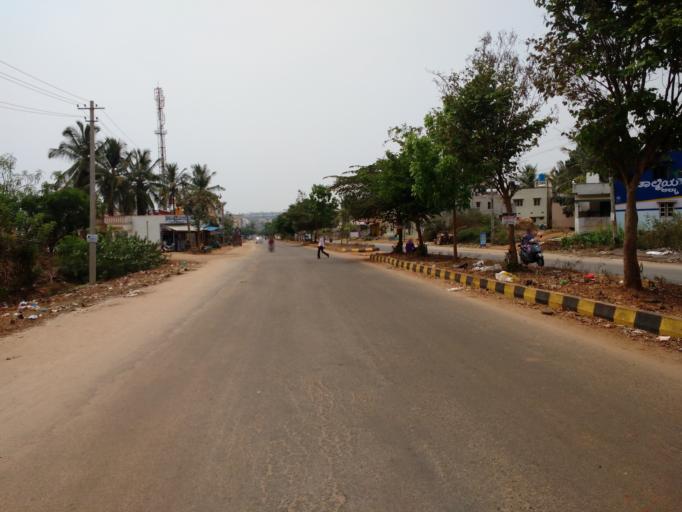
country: IN
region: Karnataka
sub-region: Hassan
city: Hassan
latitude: 13.0230
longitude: 76.1122
